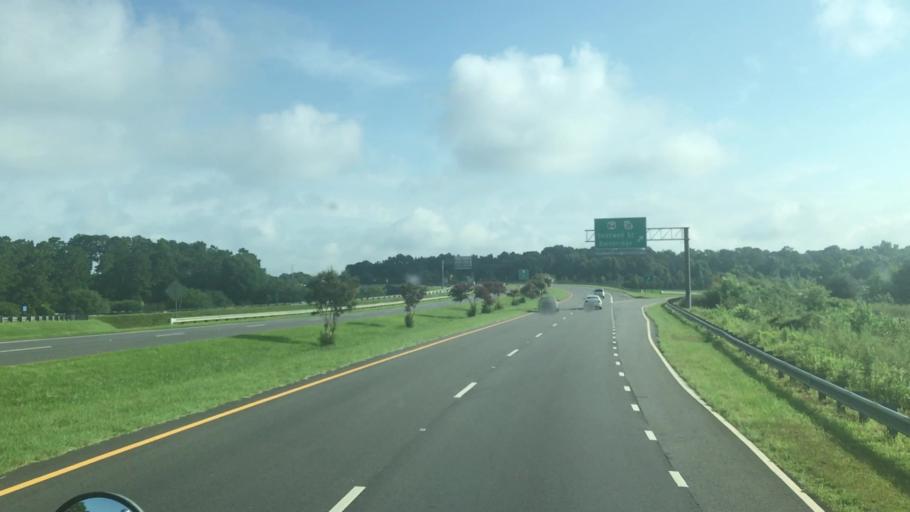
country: US
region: Georgia
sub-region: Decatur County
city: Bainbridge
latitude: 30.9009
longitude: -84.5874
